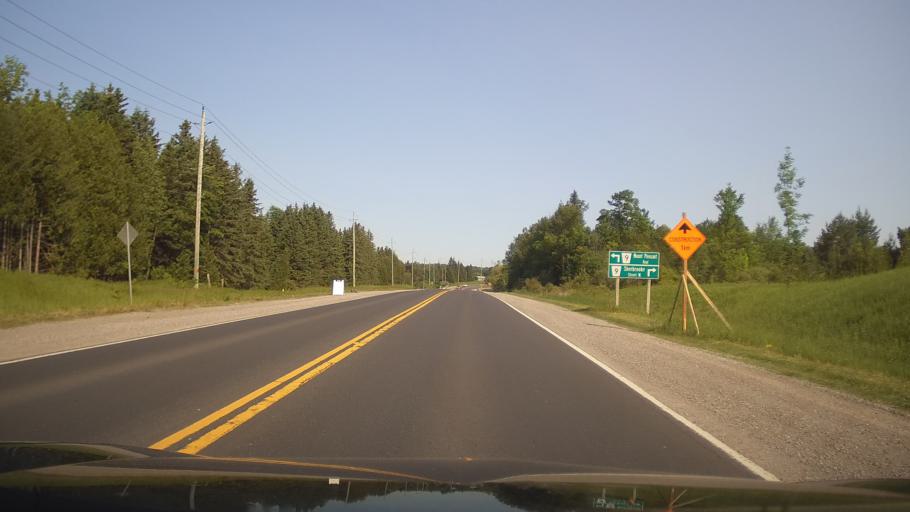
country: CA
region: Ontario
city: Peterborough
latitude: 44.2749
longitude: -78.4136
